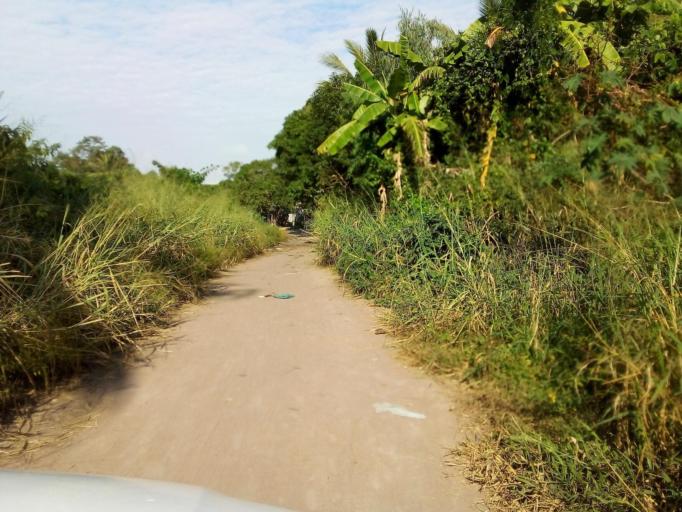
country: MZ
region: Zambezia
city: Quelimane
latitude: -17.6150
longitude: 36.8231
